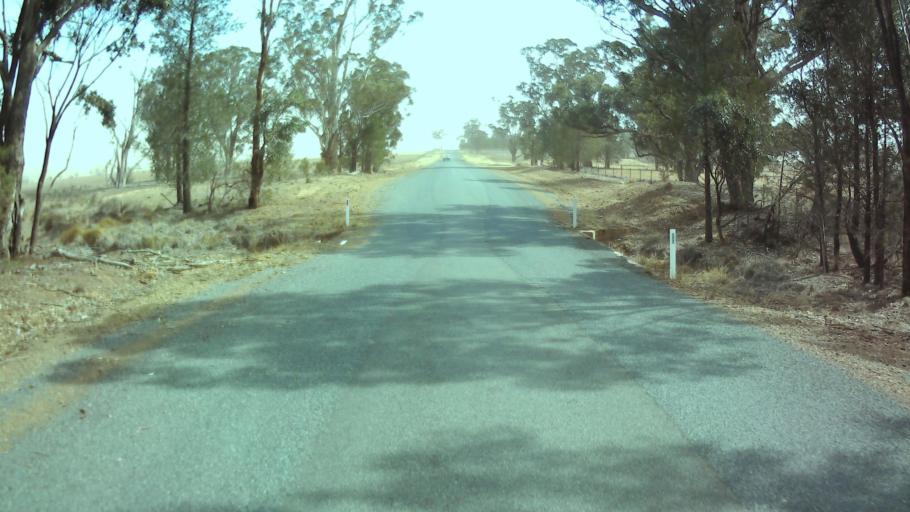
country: AU
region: New South Wales
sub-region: Weddin
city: Grenfell
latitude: -33.7516
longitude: 147.9906
